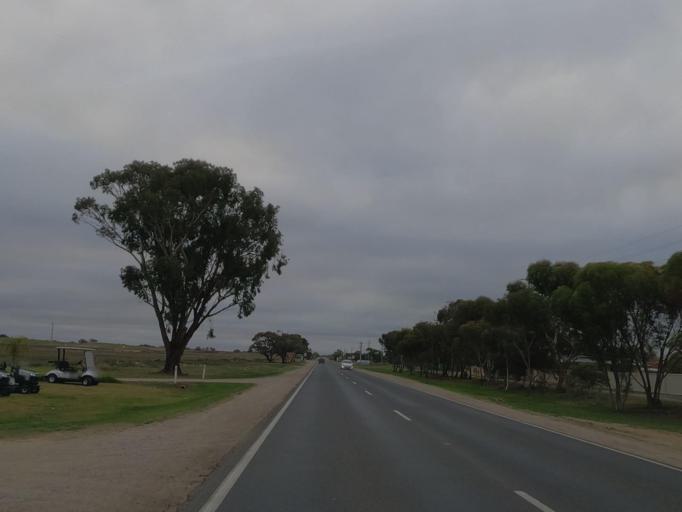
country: AU
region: Victoria
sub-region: Swan Hill
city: Swan Hill
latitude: -35.4535
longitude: 143.6268
